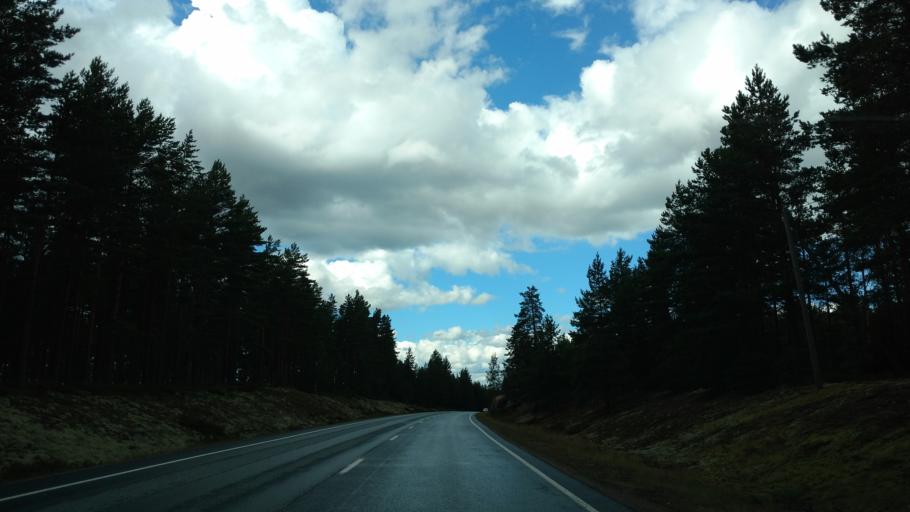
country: FI
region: Varsinais-Suomi
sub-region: Salo
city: Muurla
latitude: 60.2956
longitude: 23.3315
